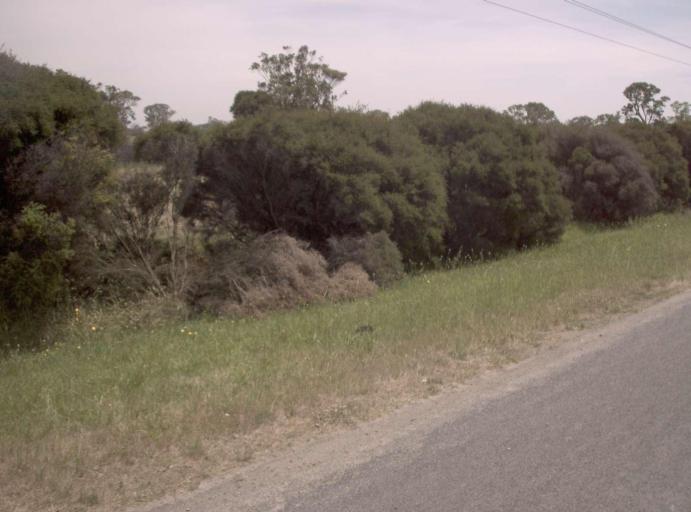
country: AU
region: Victoria
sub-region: Frankston
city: Skye
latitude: -38.0854
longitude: 145.2378
